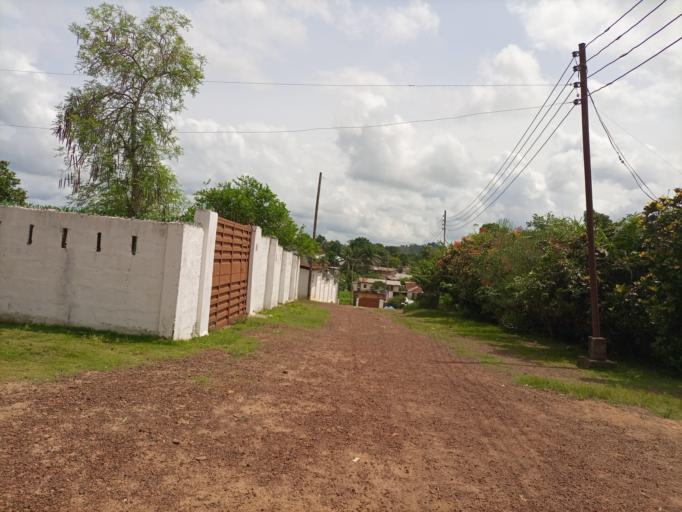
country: SL
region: Southern Province
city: Bo
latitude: 7.9591
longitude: -11.7583
